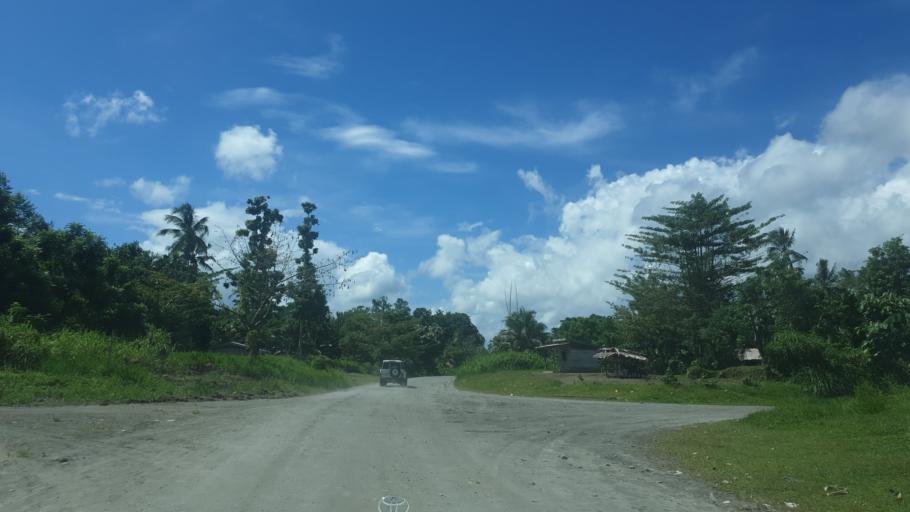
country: PG
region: Bougainville
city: Panguna
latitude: -6.6600
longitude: 155.4461
